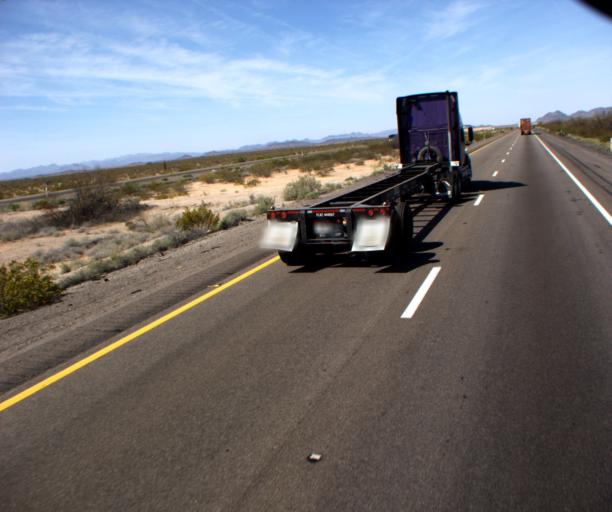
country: US
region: Arizona
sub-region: La Paz County
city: Salome
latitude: 33.5929
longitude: -113.5098
